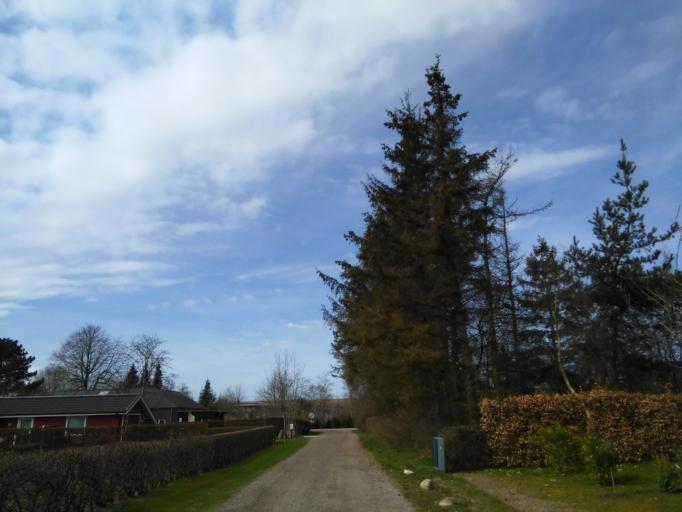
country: DK
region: Central Jutland
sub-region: Arhus Kommune
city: Malling
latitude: 55.9722
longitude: 10.2503
